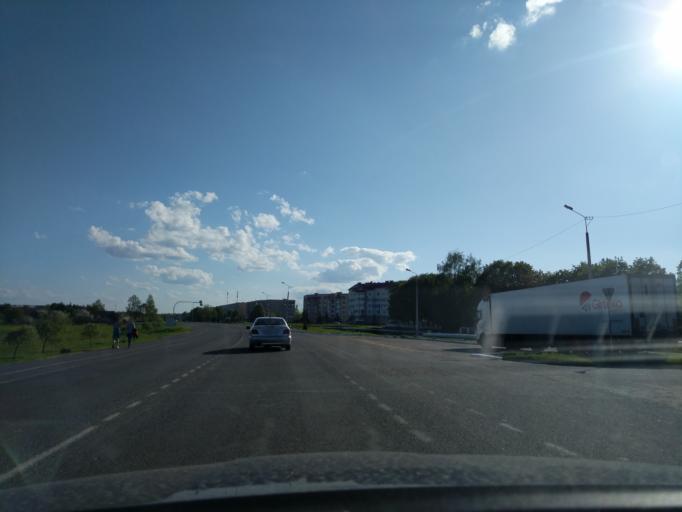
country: BY
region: Minsk
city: Myadzyel
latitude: 54.8732
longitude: 26.9389
